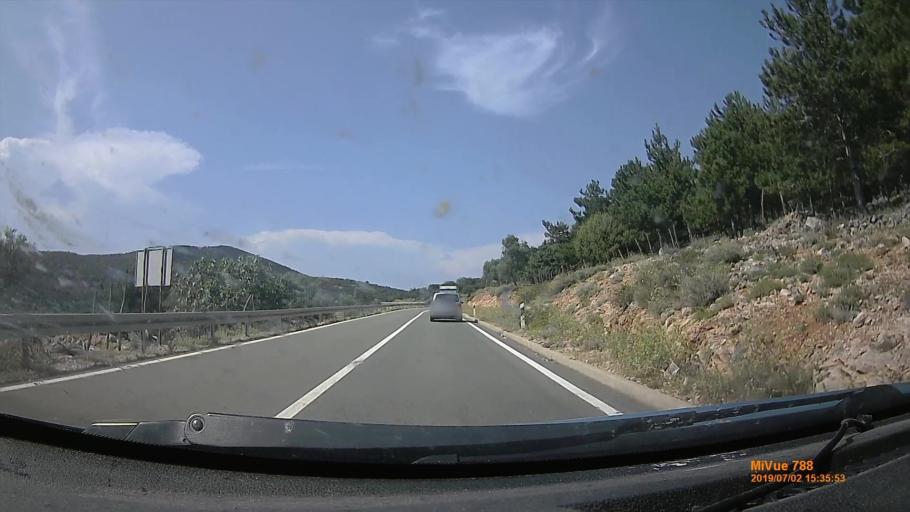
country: HR
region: Primorsko-Goranska
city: Cres
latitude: 44.9803
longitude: 14.4113
